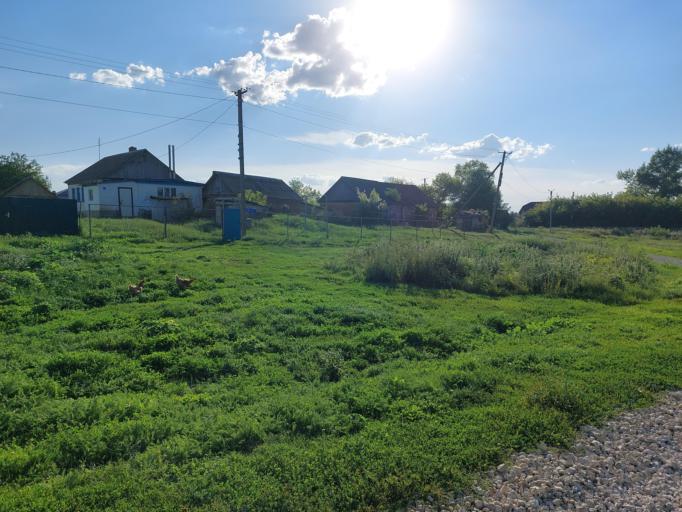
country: RU
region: Lipetsk
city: Terbuny
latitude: 52.2760
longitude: 38.1946
